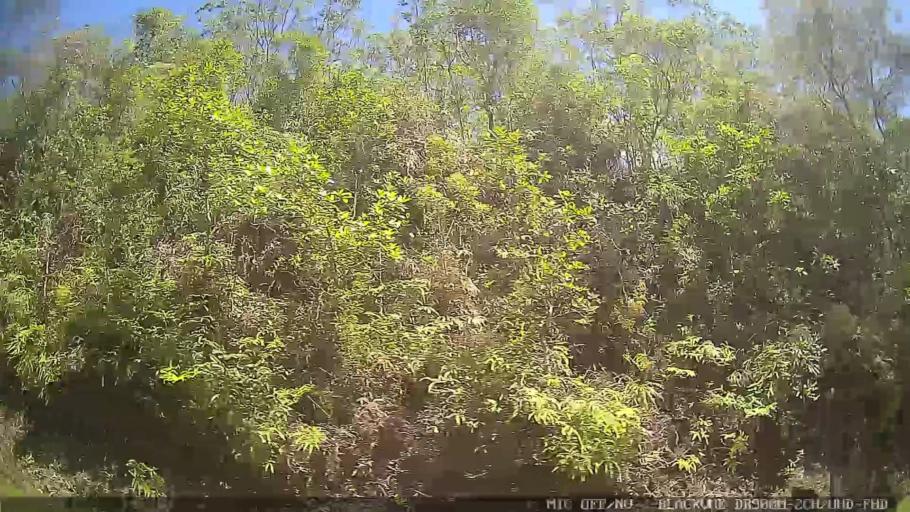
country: BR
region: Sao Paulo
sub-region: Mogi das Cruzes
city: Mogi das Cruzes
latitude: -23.6771
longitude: -46.1996
